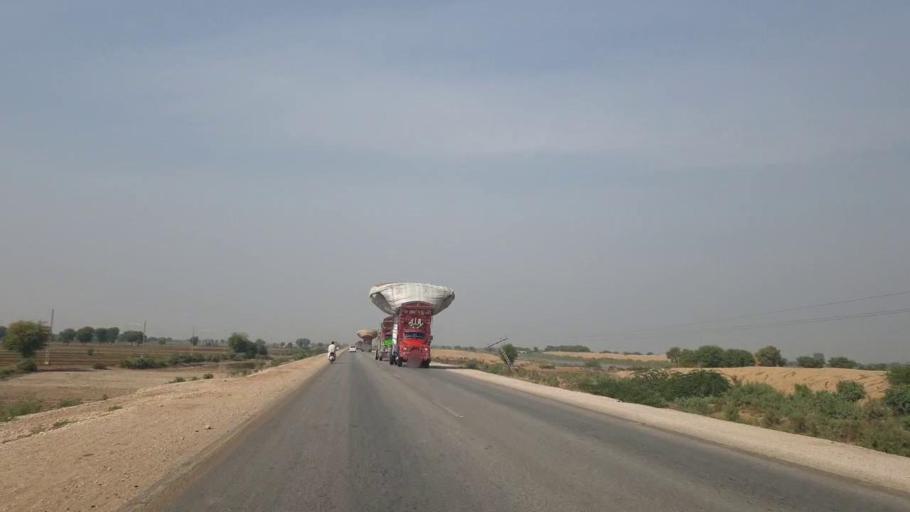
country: PK
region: Sindh
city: Sann
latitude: 26.0700
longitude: 68.0994
